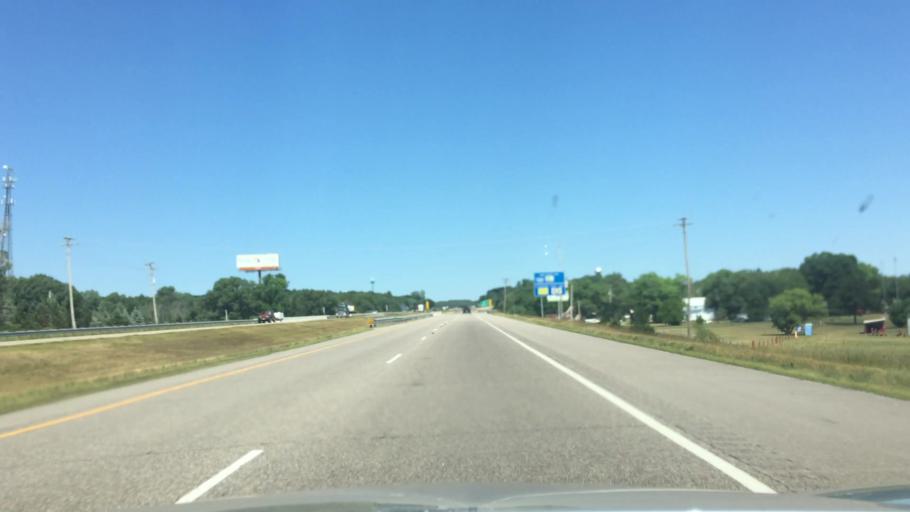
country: US
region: Wisconsin
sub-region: Marquette County
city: Westfield
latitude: 44.0263
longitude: -89.5204
